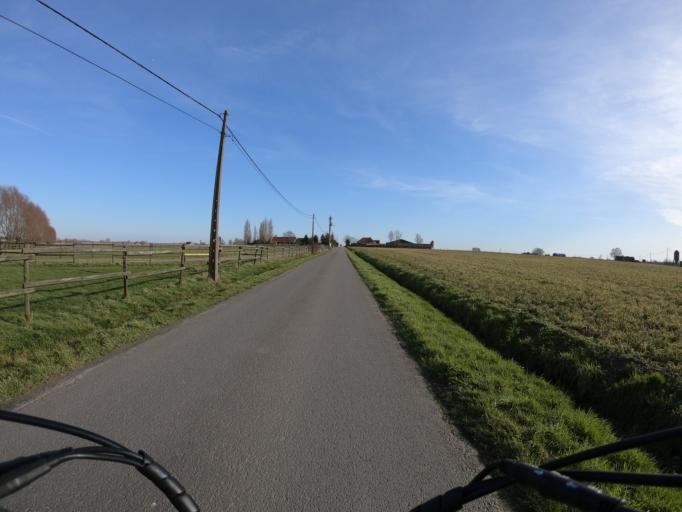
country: BE
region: Flanders
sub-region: Provincie West-Vlaanderen
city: Moorslede
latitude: 50.8820
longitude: 3.0725
